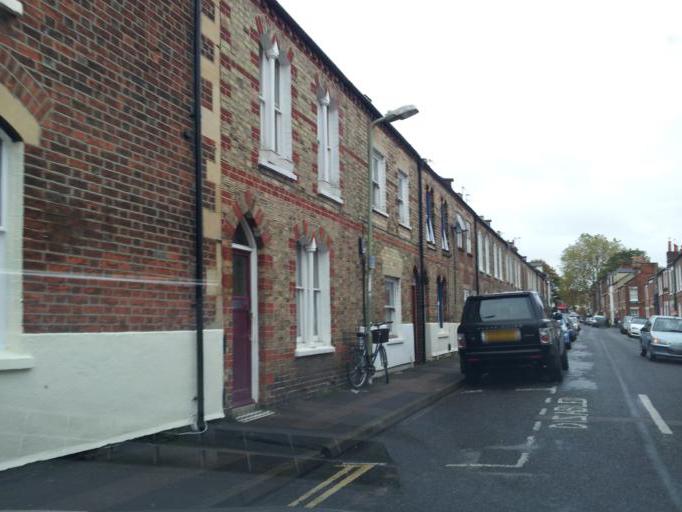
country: GB
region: England
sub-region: Oxfordshire
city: Oxford
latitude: 51.7588
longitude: -1.2701
